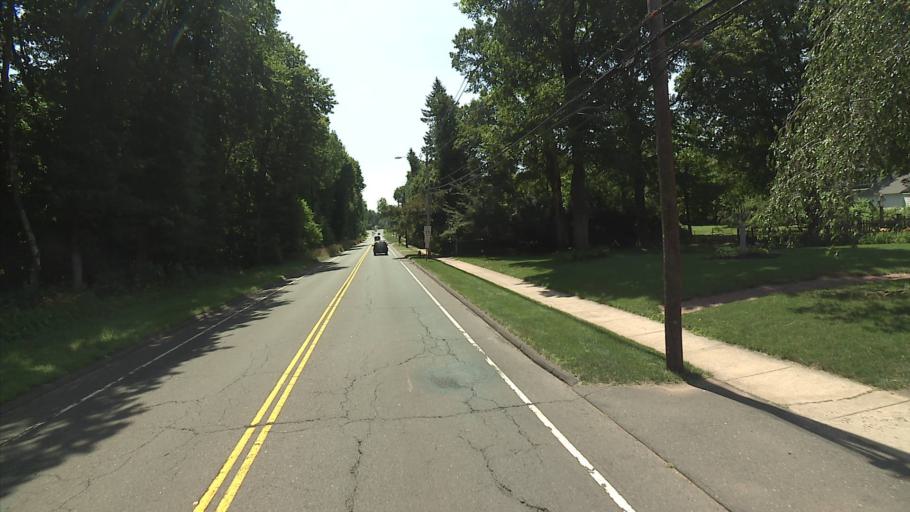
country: US
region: Connecticut
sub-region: Hartford County
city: New Britain
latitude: 41.6511
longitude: -72.7942
